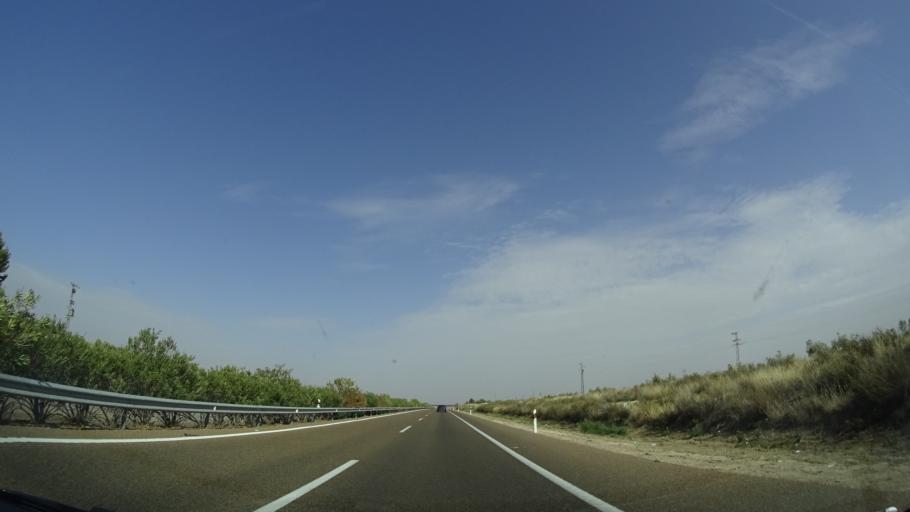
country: ES
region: Extremadura
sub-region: Provincia de Badajoz
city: Villafranca de los Barros
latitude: 38.5050
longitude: -6.3538
